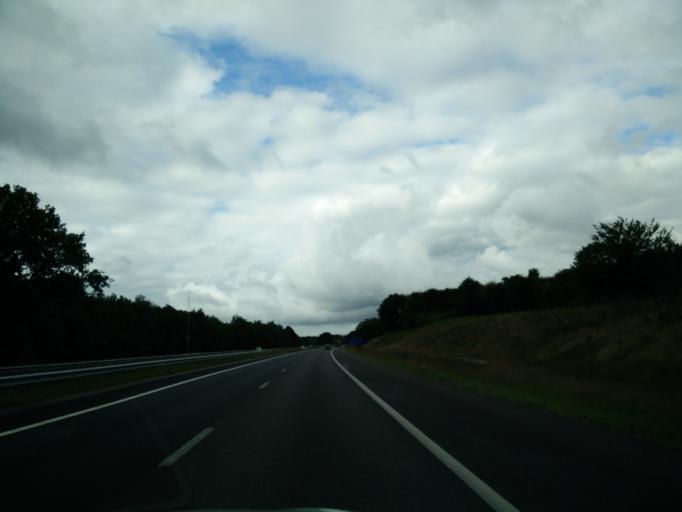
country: NL
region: Drenthe
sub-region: Gemeente Westerveld
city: Dwingeloo
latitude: 52.8219
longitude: 6.4680
